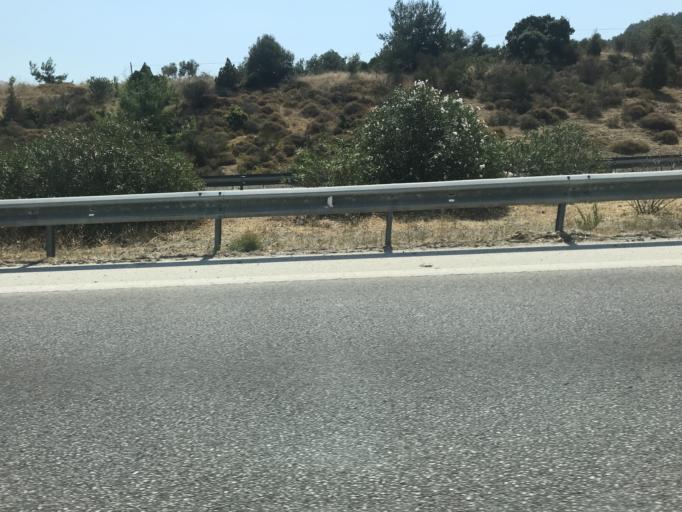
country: TR
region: Izmir
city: Urla
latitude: 38.3251
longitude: 26.8052
